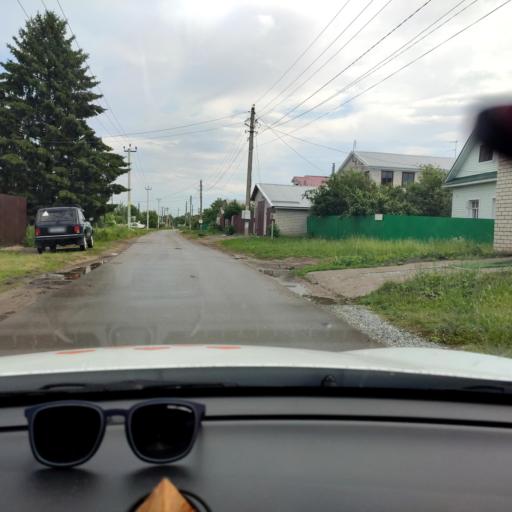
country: RU
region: Tatarstan
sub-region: Zelenodol'skiy Rayon
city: Vasil'yevo
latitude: 55.8267
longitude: 48.7231
